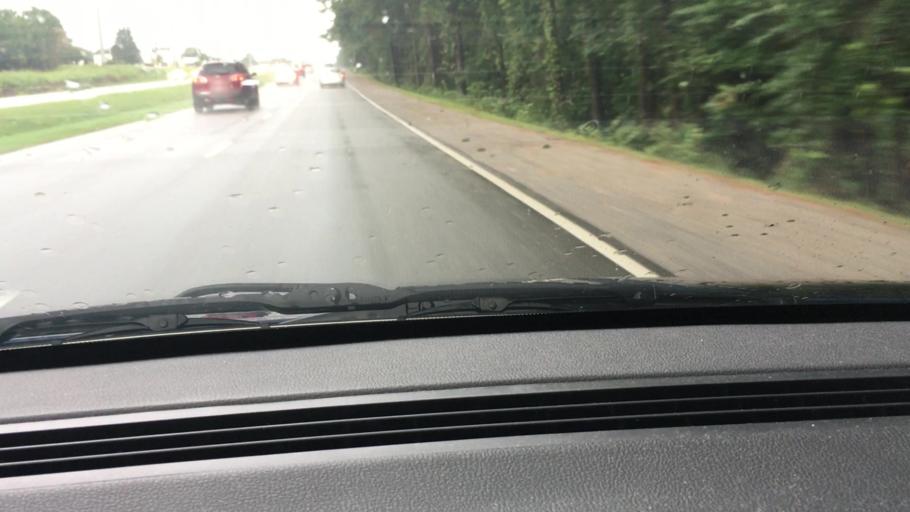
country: US
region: Alabama
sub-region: Tuscaloosa County
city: Northport
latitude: 33.2348
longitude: -87.5461
